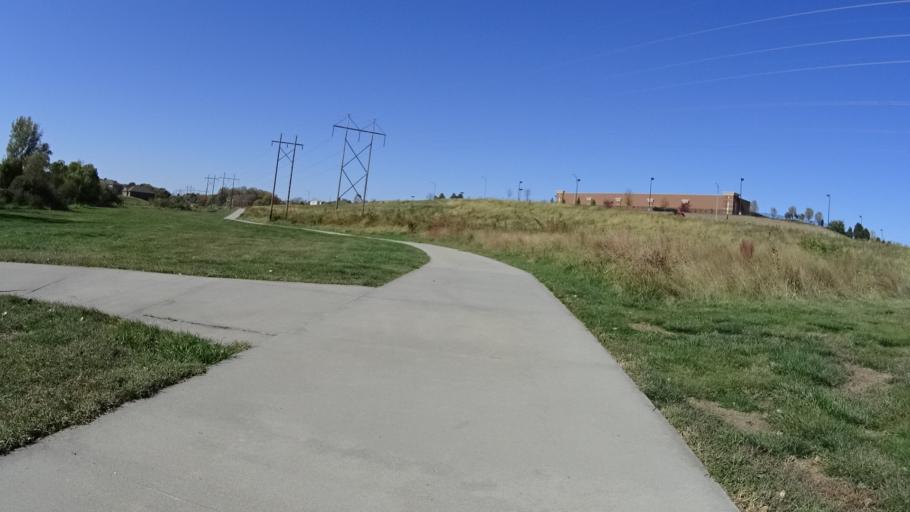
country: US
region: Nebraska
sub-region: Sarpy County
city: La Vista
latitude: 41.1687
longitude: -96.0189
